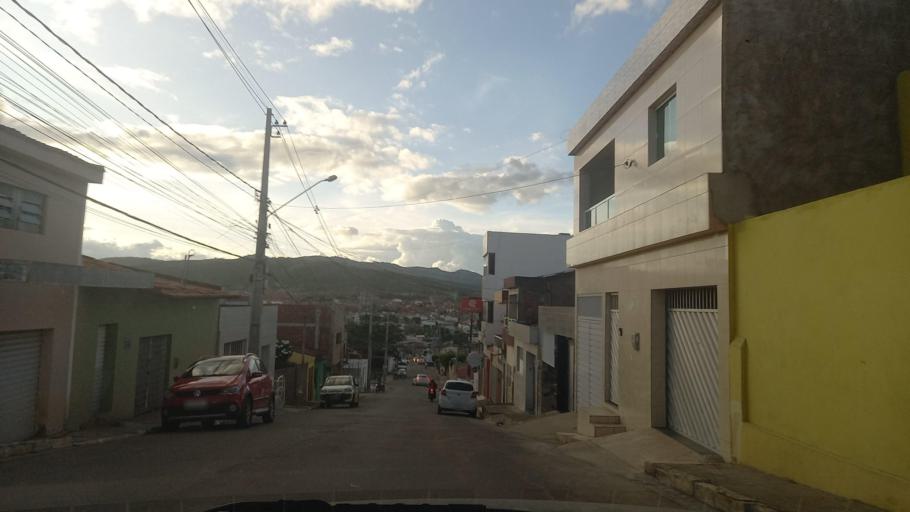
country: BR
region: Pernambuco
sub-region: Bezerros
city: Bezerros
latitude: -8.2393
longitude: -35.7497
